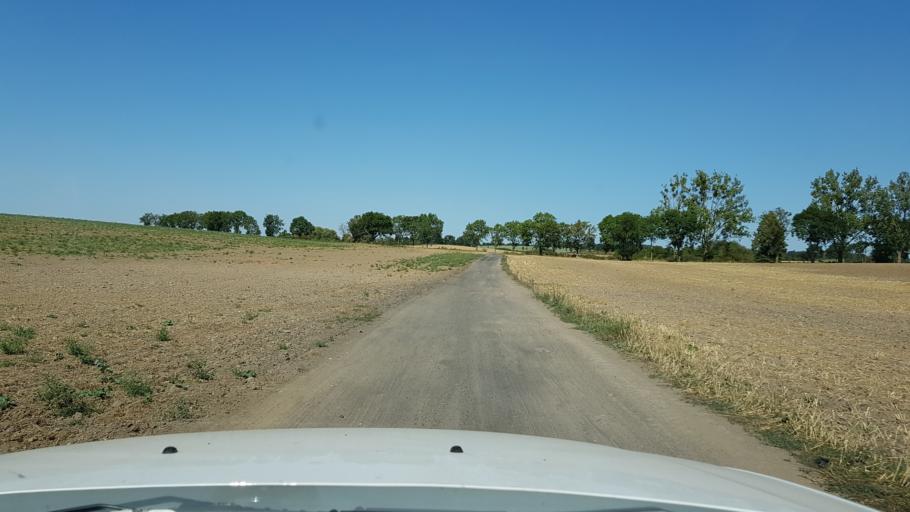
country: PL
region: West Pomeranian Voivodeship
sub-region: Powiat gryfinski
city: Moryn
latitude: 52.8663
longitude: 14.3549
